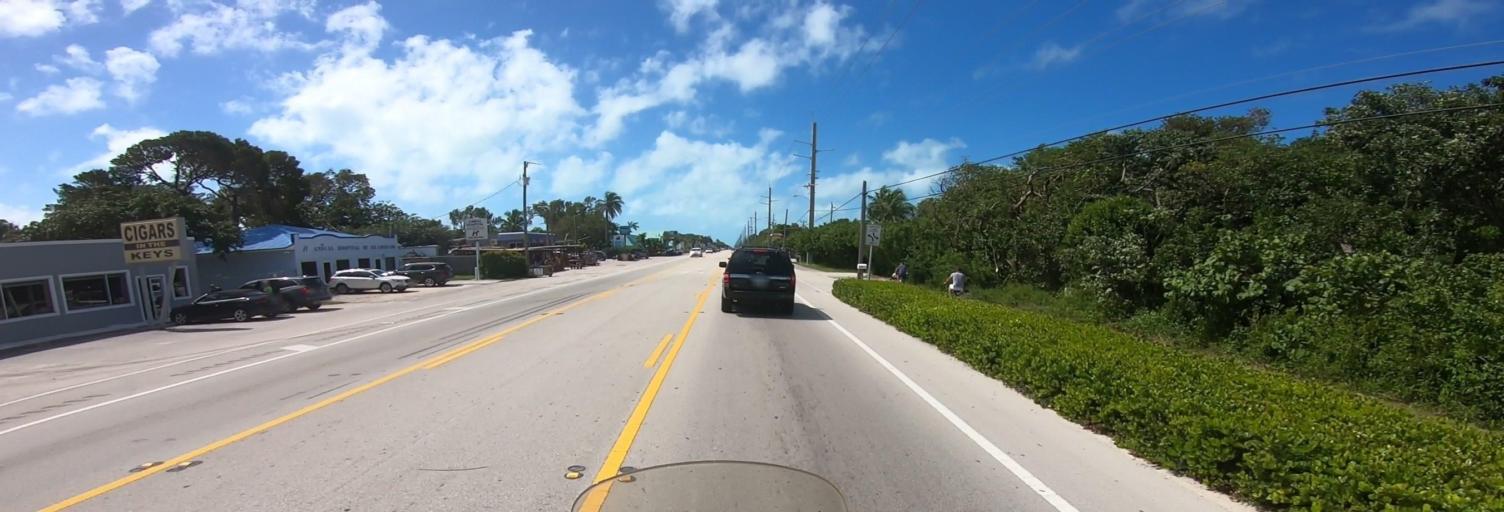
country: US
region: Florida
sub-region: Monroe County
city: Islamorada
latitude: 24.9285
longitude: -80.6237
